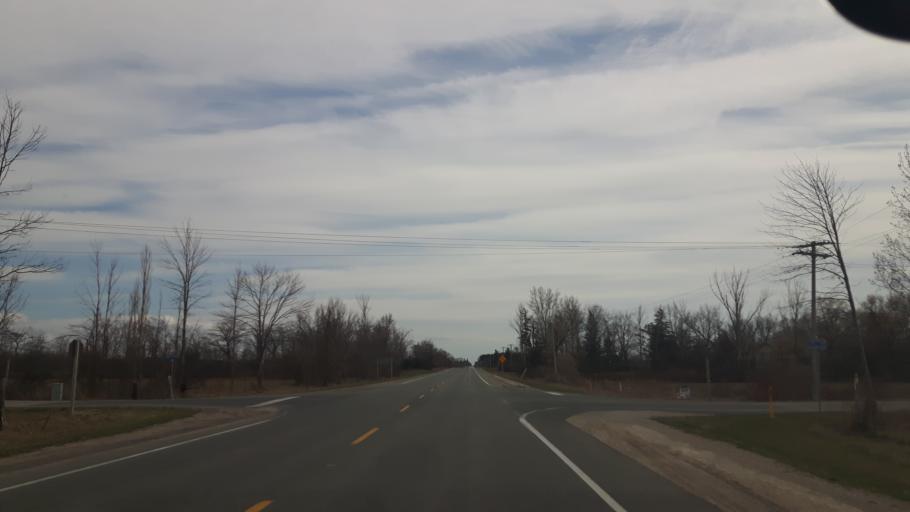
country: CA
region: Ontario
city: Goderich
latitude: 43.7173
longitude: -81.7058
